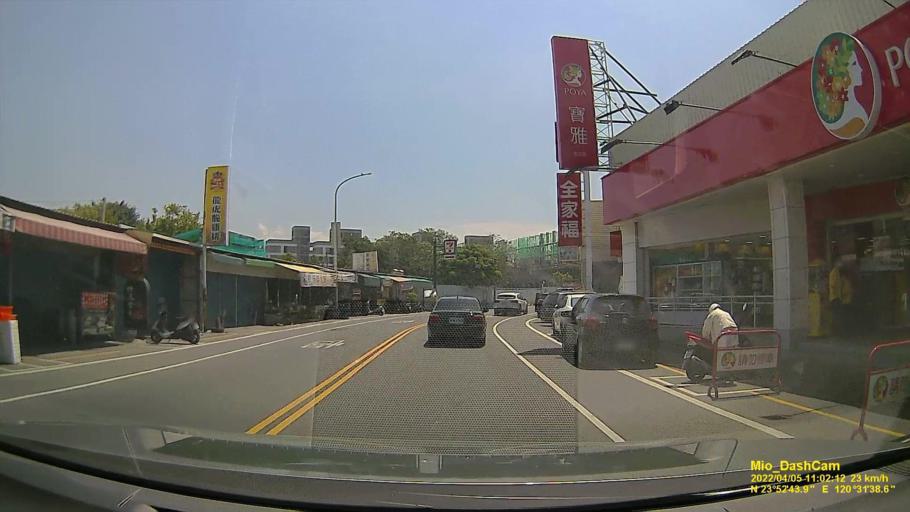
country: TW
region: Taiwan
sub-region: Nantou
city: Nantou
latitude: 23.8789
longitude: 120.5274
